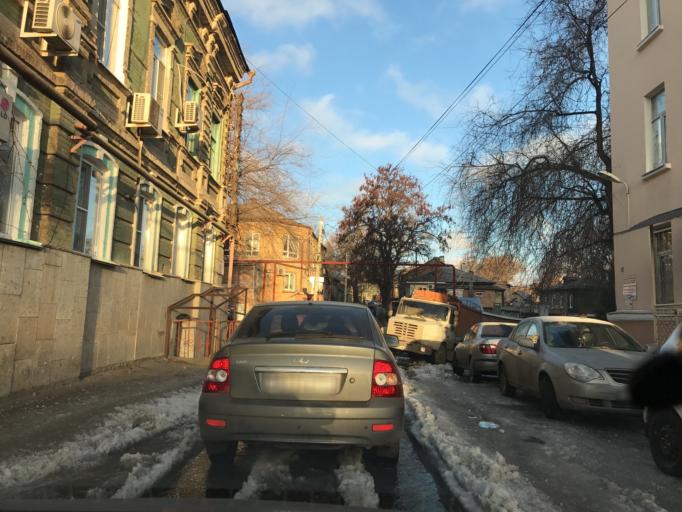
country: RU
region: Rostov
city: Rostov-na-Donu
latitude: 47.2184
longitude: 39.6847
